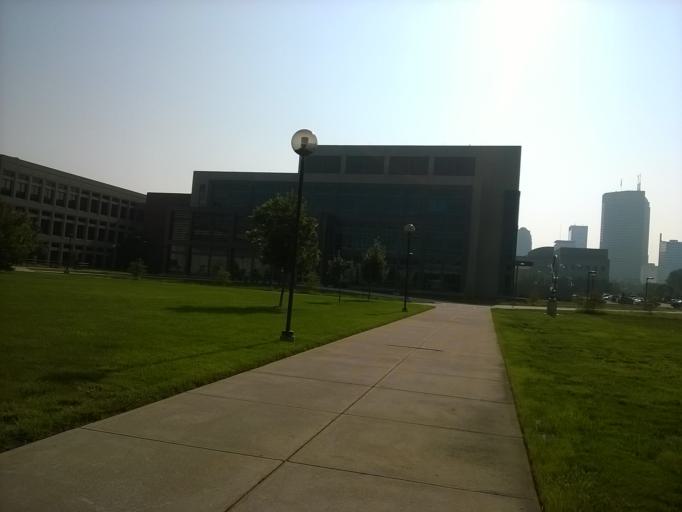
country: US
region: Indiana
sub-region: Marion County
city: Indianapolis
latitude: 39.7724
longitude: -86.1718
